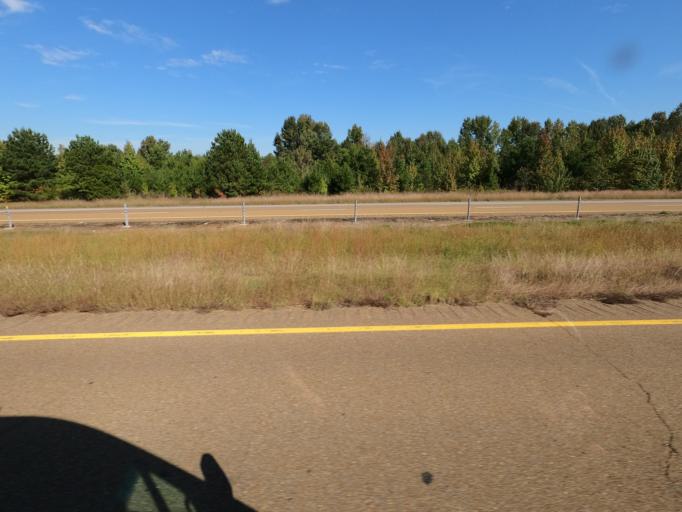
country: US
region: Tennessee
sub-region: Shelby County
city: Lakeland
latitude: 35.3074
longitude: -89.8008
